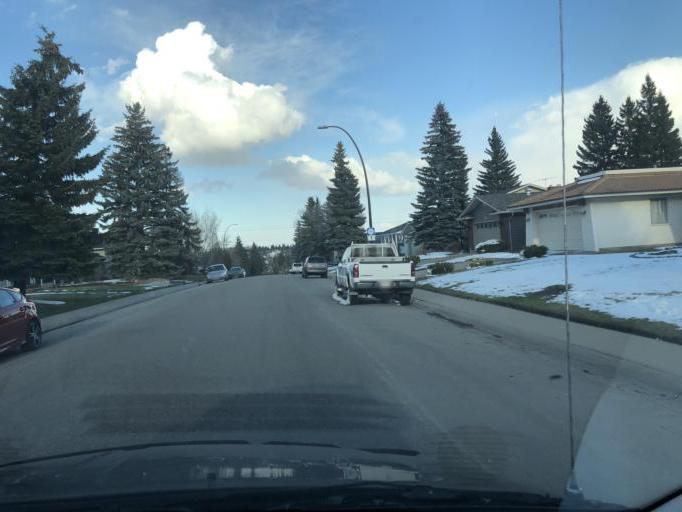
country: CA
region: Alberta
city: Calgary
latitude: 50.9428
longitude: -114.0383
